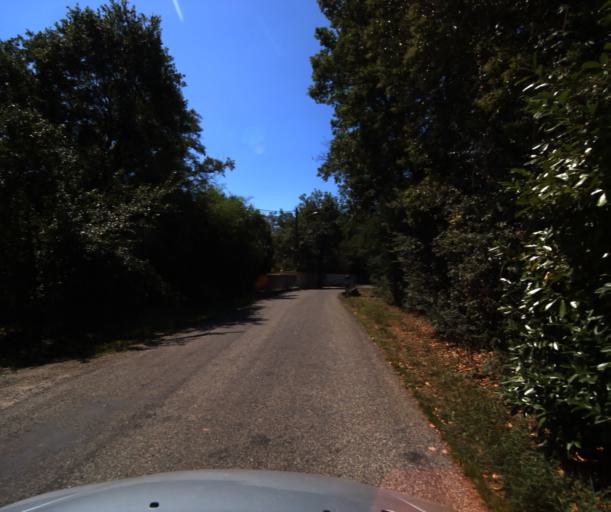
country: FR
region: Midi-Pyrenees
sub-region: Departement de la Haute-Garonne
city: Muret
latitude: 43.4573
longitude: 1.3519
